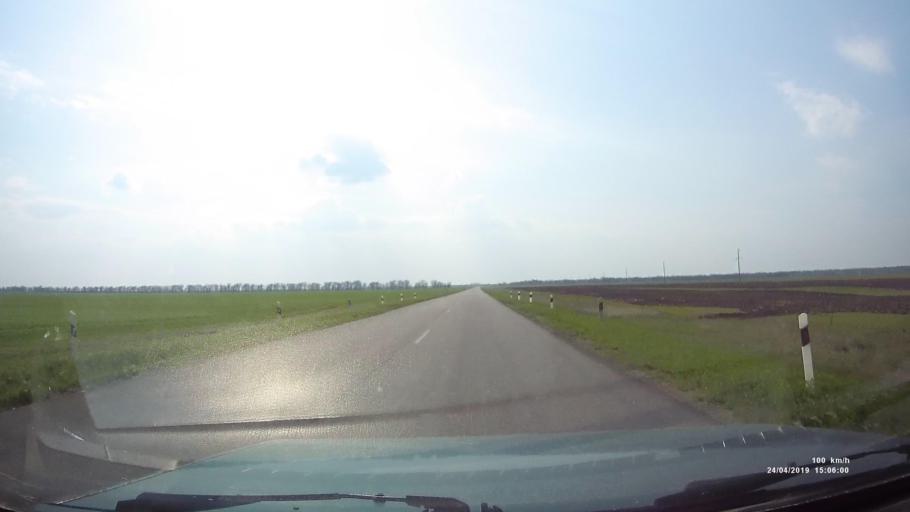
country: RU
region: Rostov
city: Remontnoye
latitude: 46.5593
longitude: 43.4368
